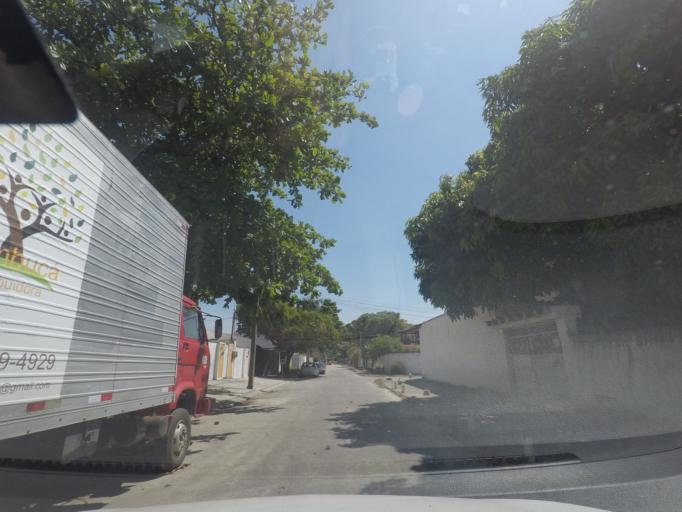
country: BR
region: Rio de Janeiro
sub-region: Niteroi
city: Niteroi
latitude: -22.9441
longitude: -43.0250
